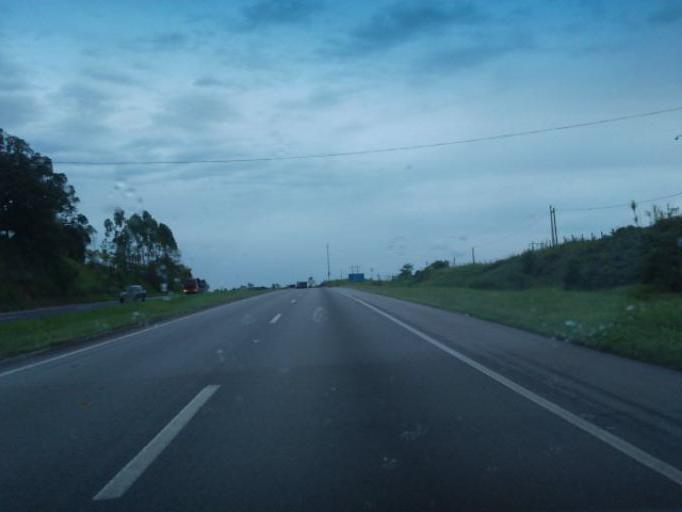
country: BR
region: Sao Paulo
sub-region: Registro
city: Registro
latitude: -24.4520
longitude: -47.8102
